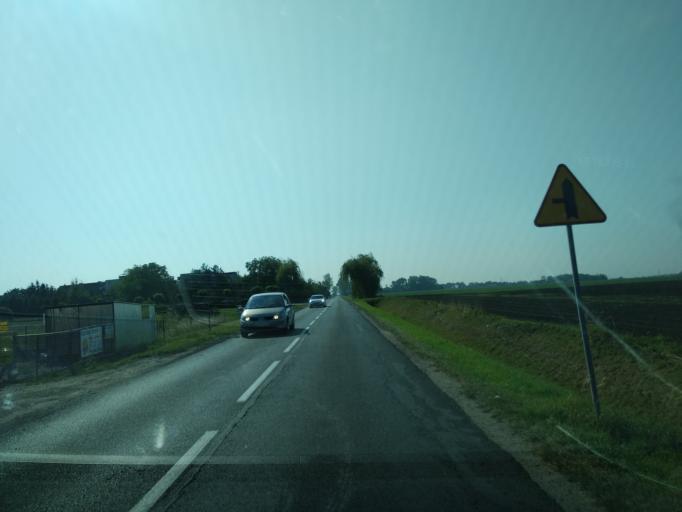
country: PL
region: Lower Silesian Voivodeship
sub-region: Powiat wroclawski
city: Zerniki Wroclawskie
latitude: 51.0350
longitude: 17.0306
